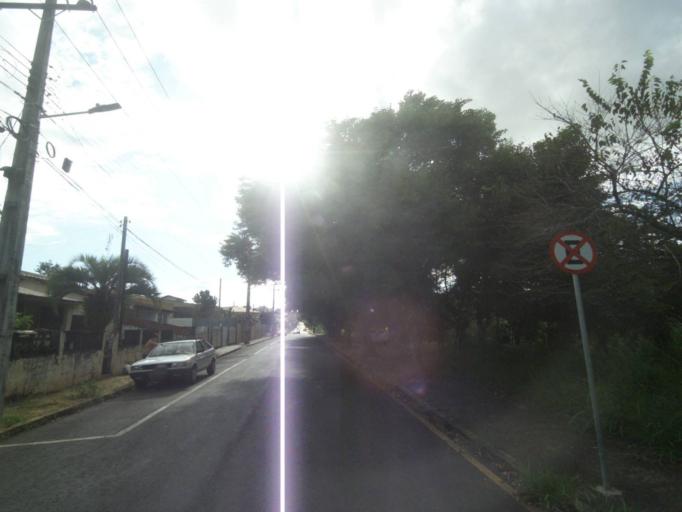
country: BR
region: Parana
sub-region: Telemaco Borba
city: Telemaco Borba
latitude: -24.3351
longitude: -50.6155
